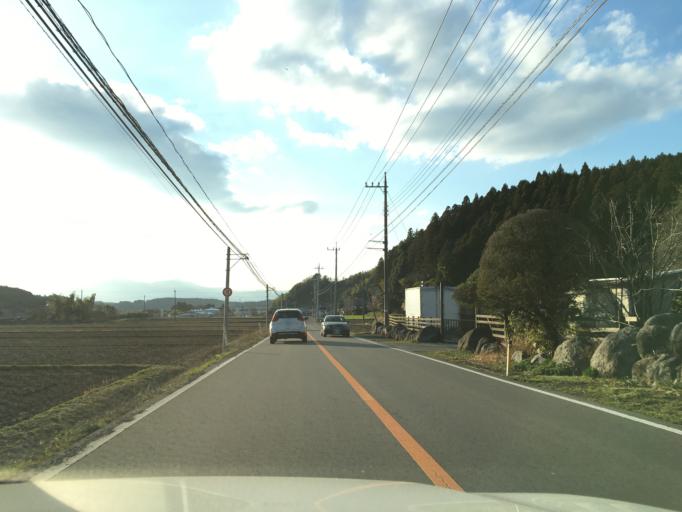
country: JP
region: Tochigi
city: Otawara
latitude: 36.8680
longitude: 140.1550
